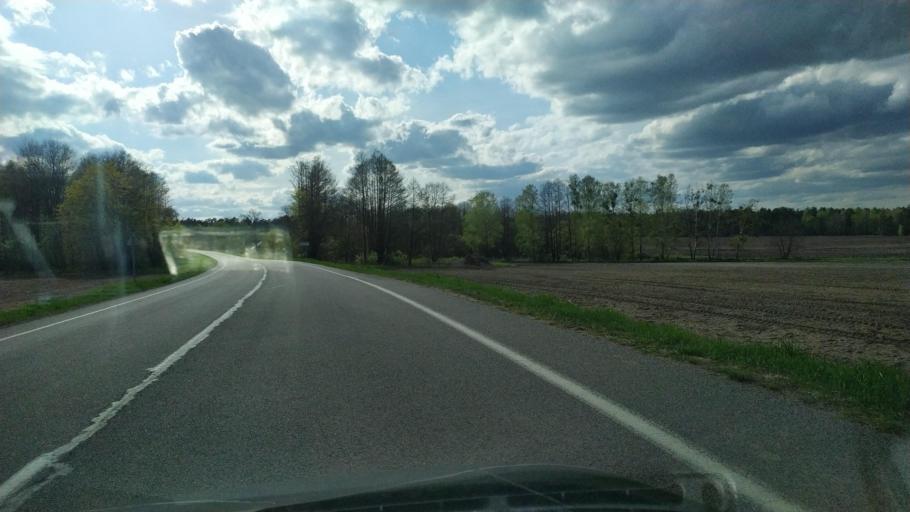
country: BY
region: Brest
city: Pruzhany
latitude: 52.7035
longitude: 24.3220
